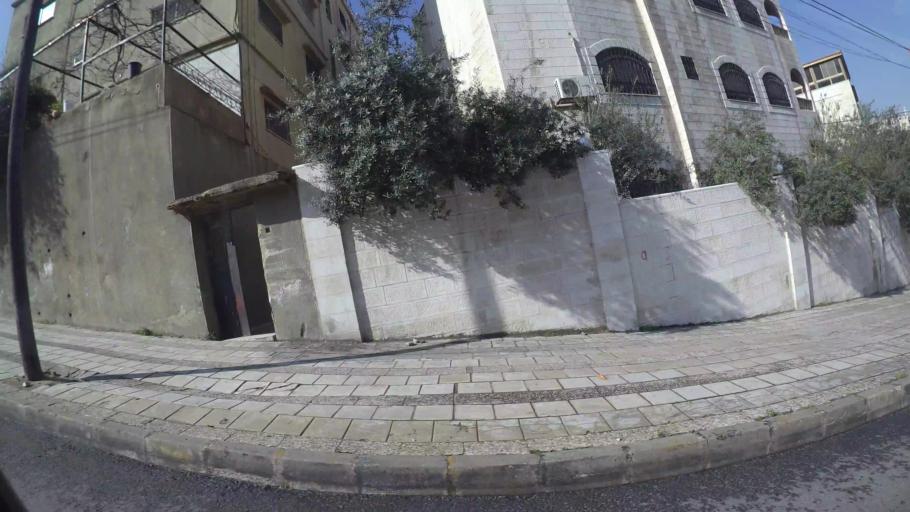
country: JO
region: Amman
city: Amman
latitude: 31.9391
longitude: 35.9092
